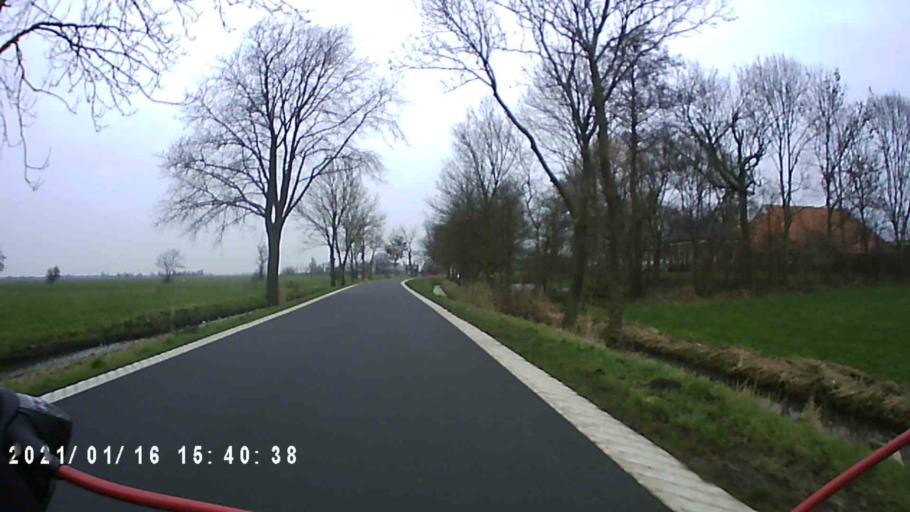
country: NL
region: Groningen
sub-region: Gemeente Groningen
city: Korrewegwijk
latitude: 53.2717
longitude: 6.5650
